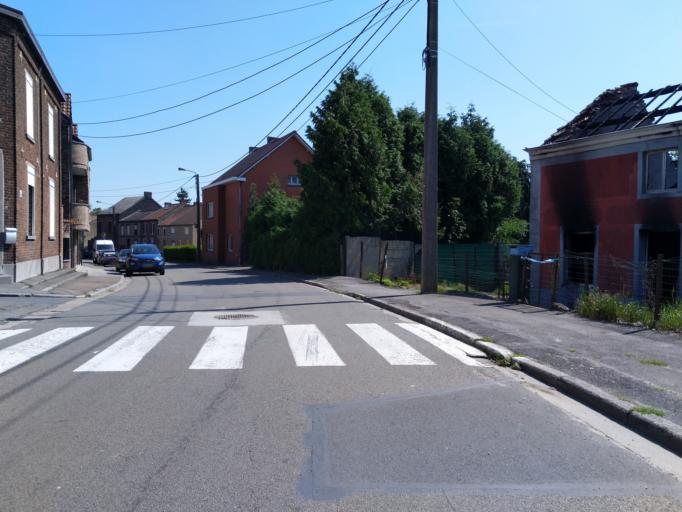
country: BE
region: Wallonia
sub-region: Province du Hainaut
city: Roeulx
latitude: 50.4756
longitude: 4.0996
